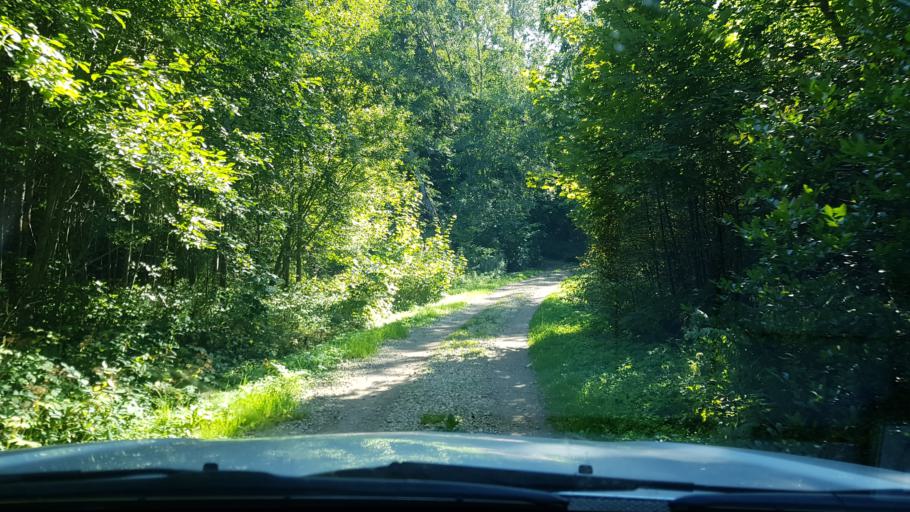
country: EE
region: Ida-Virumaa
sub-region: Sillamaee linn
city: Sillamae
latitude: 59.3981
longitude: 27.8787
